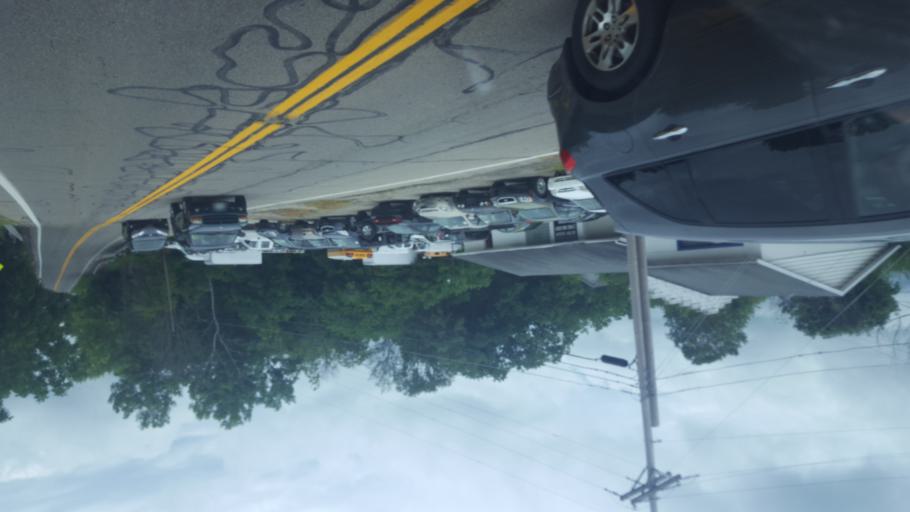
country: US
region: Ohio
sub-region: Pickaway County
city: South Bloomfield
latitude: 39.7215
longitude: -83.0199
